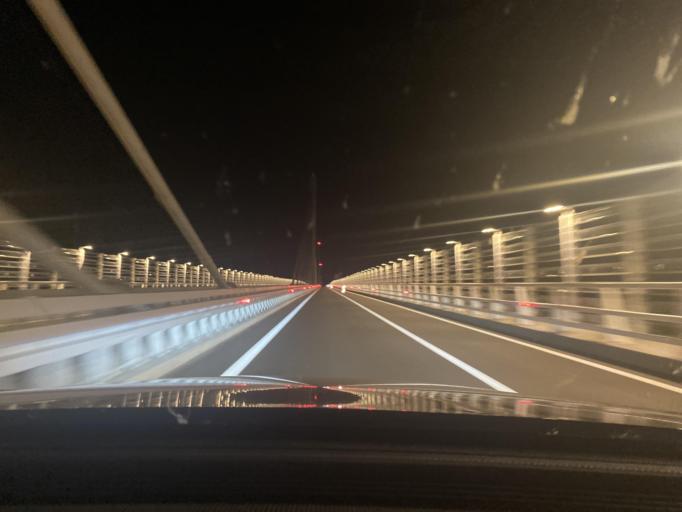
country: BA
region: Federation of Bosnia and Herzegovina
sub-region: Hercegovacko-Bosanski Kanton
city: Neum
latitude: 42.9364
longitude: 17.5404
